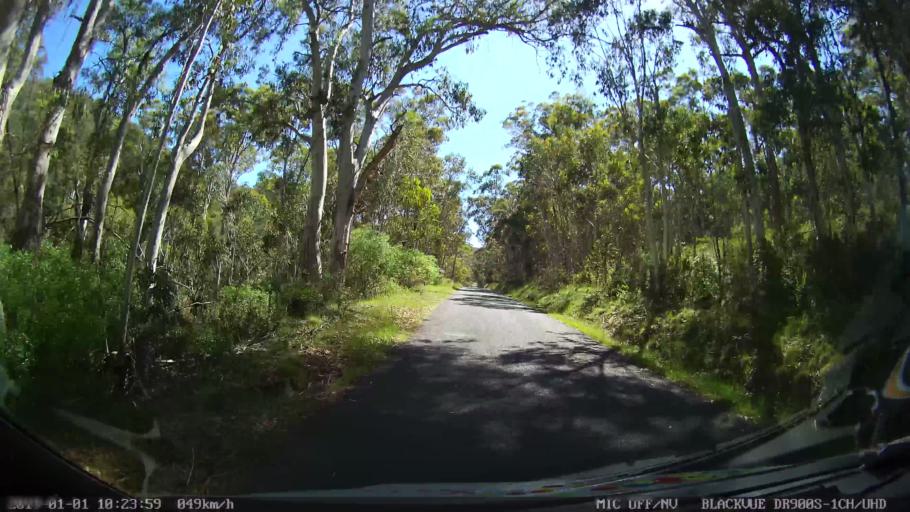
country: AU
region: New South Wales
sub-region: Snowy River
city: Jindabyne
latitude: -36.0740
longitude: 148.2161
